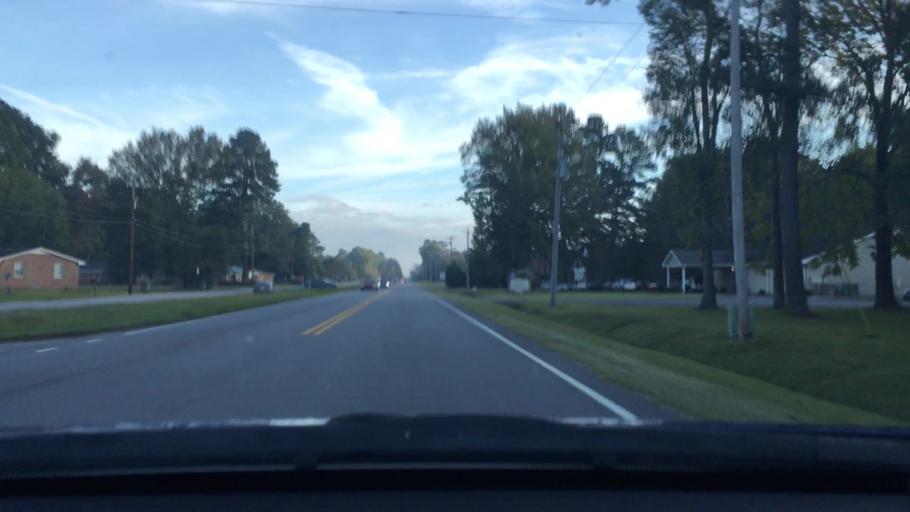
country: US
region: South Carolina
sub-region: Sumter County
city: Sumter
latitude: 33.9274
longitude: -80.3263
